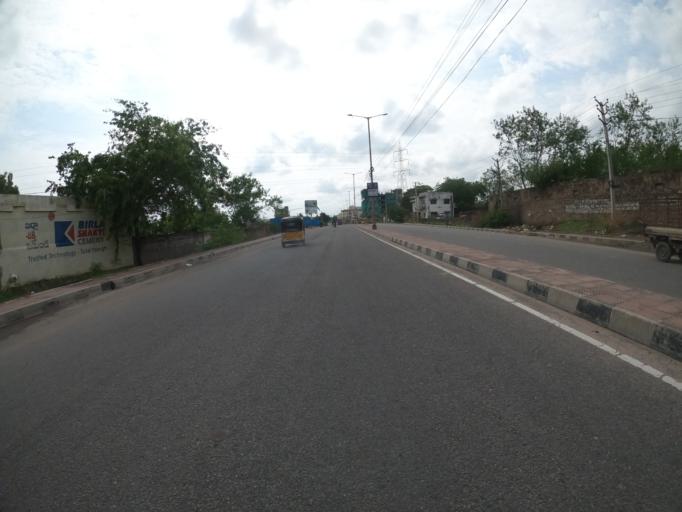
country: IN
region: Telangana
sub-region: Hyderabad
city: Hyderabad
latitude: 17.3819
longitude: 78.3657
